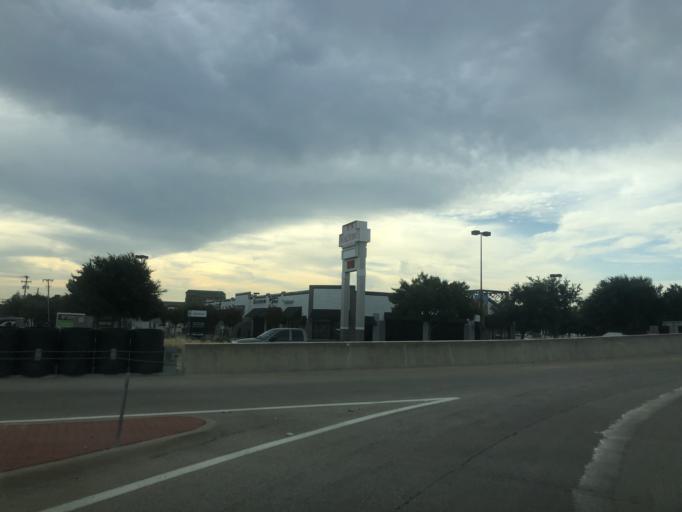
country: US
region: Texas
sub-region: Tarrant County
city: Grapevine
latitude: 32.9311
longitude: -97.0926
